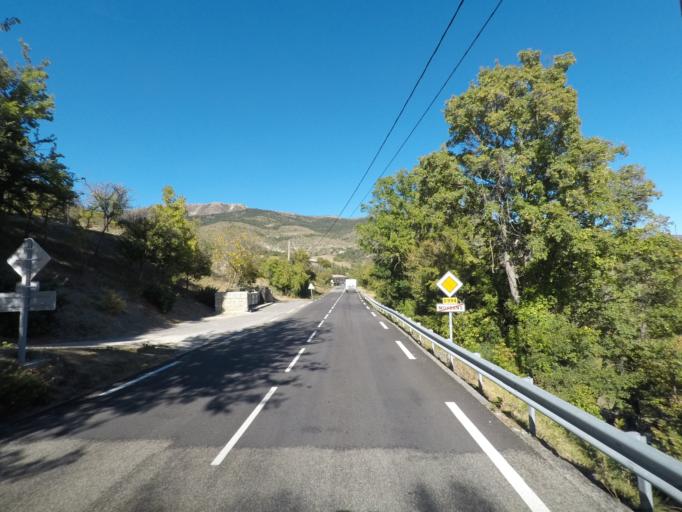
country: FR
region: Provence-Alpes-Cote d'Azur
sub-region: Departement des Hautes-Alpes
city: Serres
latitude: 44.3999
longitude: 5.5051
